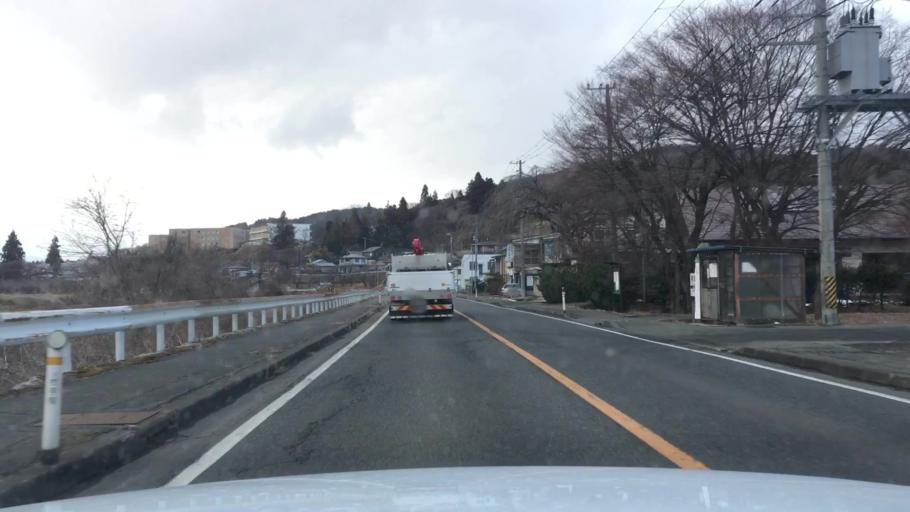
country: JP
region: Iwate
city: Morioka-shi
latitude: 39.6844
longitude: 141.1822
